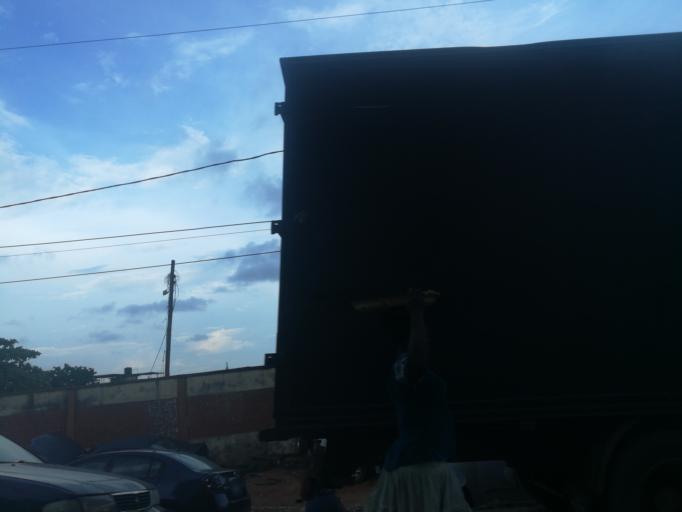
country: NG
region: Lagos
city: Somolu
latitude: 6.5592
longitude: 3.3715
